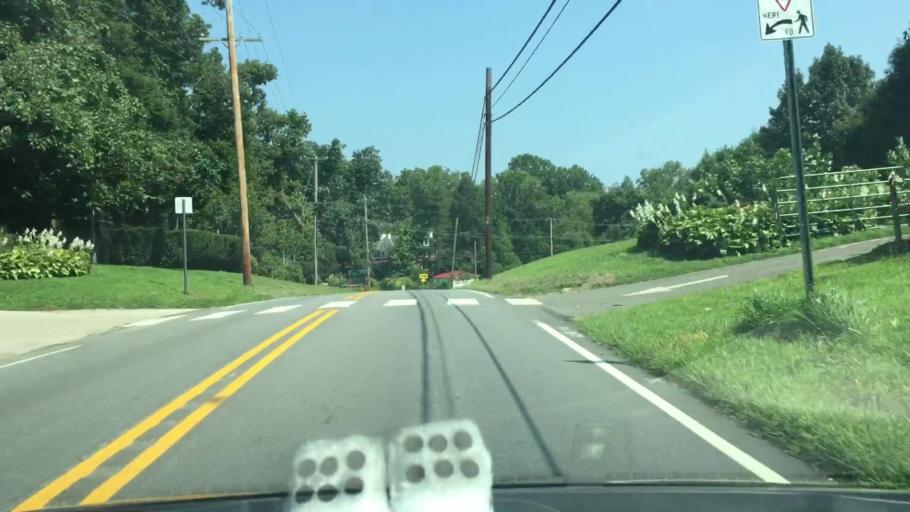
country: US
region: Pennsylvania
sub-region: Delaware County
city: Village Green-Green Ridge
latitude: 39.8825
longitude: -75.4134
